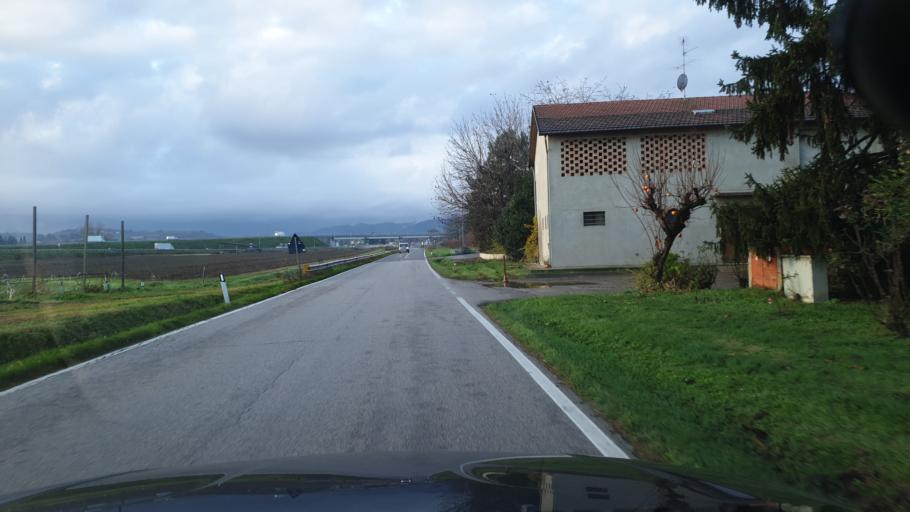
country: IT
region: Emilia-Romagna
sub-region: Provincia di Bologna
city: Crespellano
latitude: 44.5203
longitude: 11.1162
